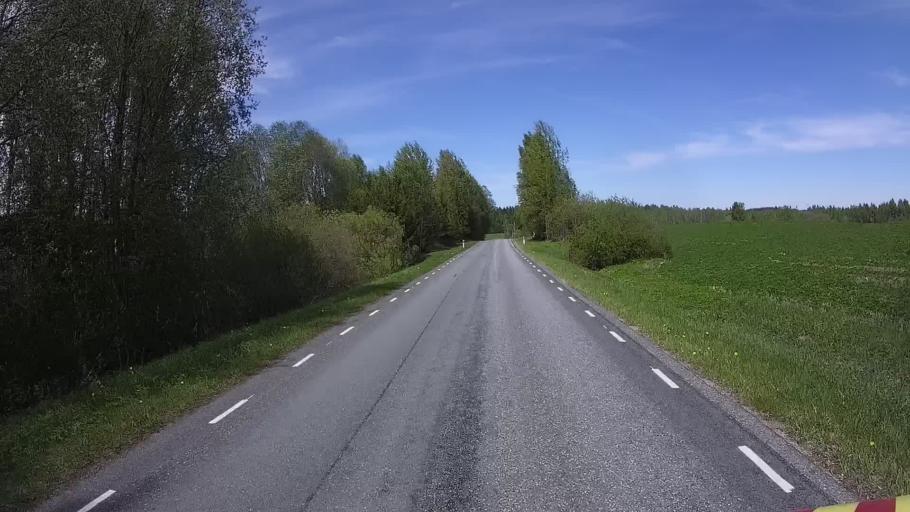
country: EE
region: Valgamaa
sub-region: Valga linn
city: Valga
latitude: 57.6604
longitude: 26.2888
